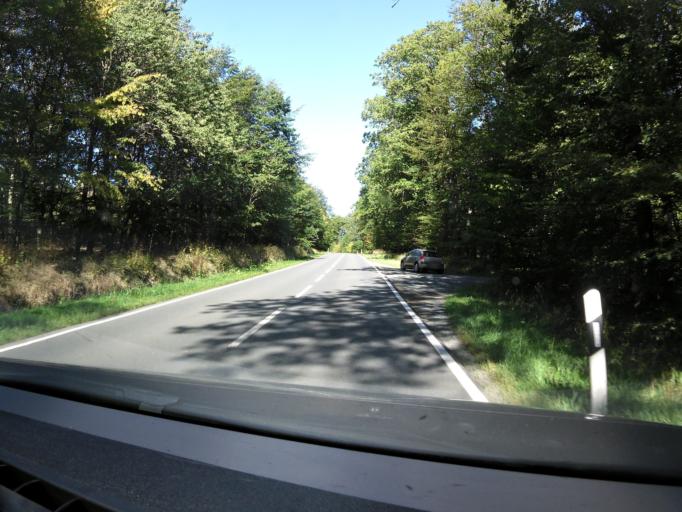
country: DE
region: Saxony-Anhalt
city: Gernrode
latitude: 51.7005
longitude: 11.1315
